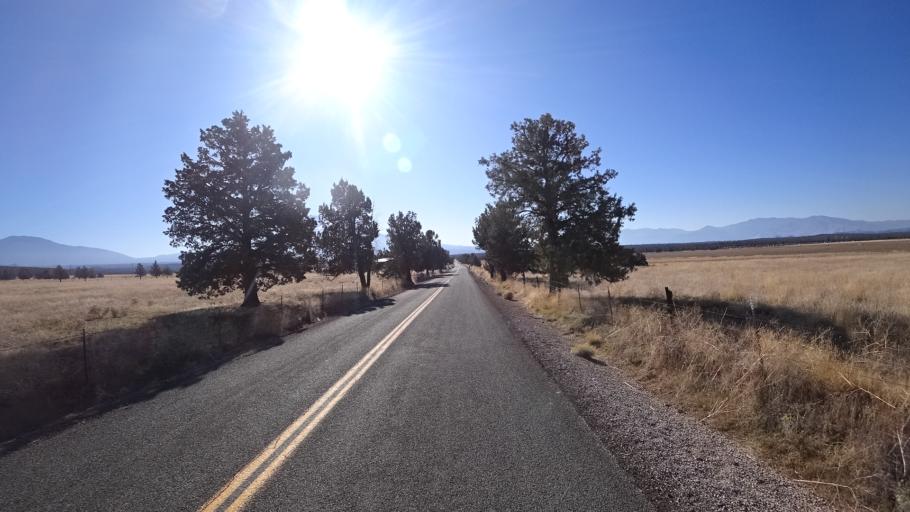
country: US
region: California
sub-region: Siskiyou County
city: Weed
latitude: 41.6008
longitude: -122.3019
